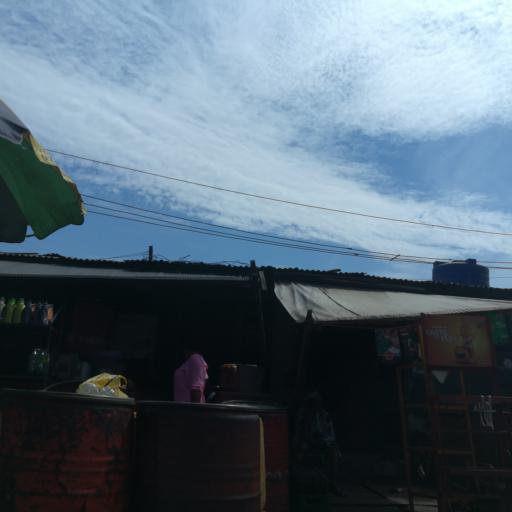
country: NG
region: Lagos
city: Lagos
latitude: 6.4649
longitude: 3.3914
